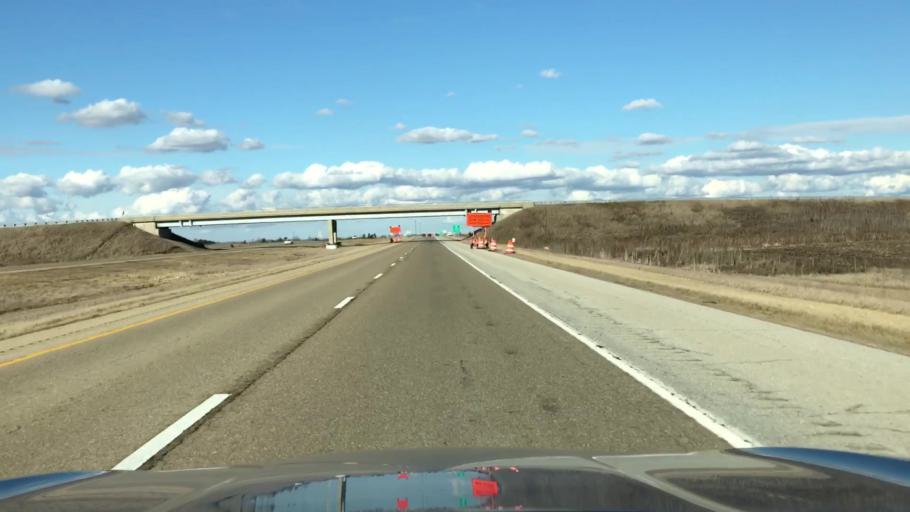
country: US
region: Illinois
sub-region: McLean County
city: Chenoa
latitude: 40.7254
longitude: -88.7370
